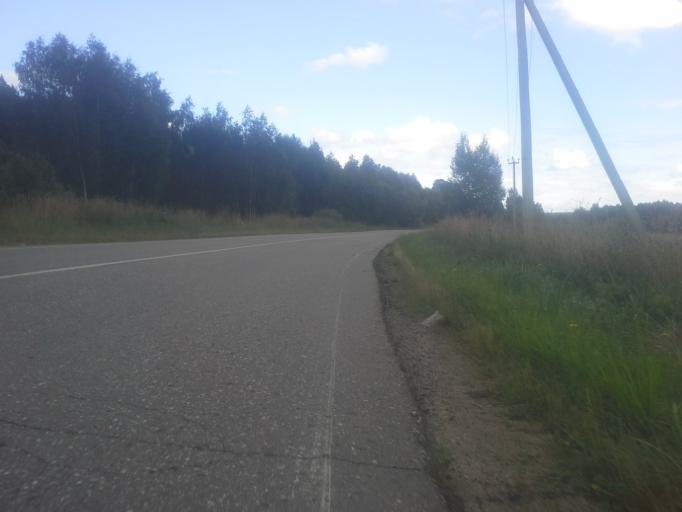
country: RU
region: Moskovskaya
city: Kolyubakino
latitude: 55.6500
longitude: 36.5839
